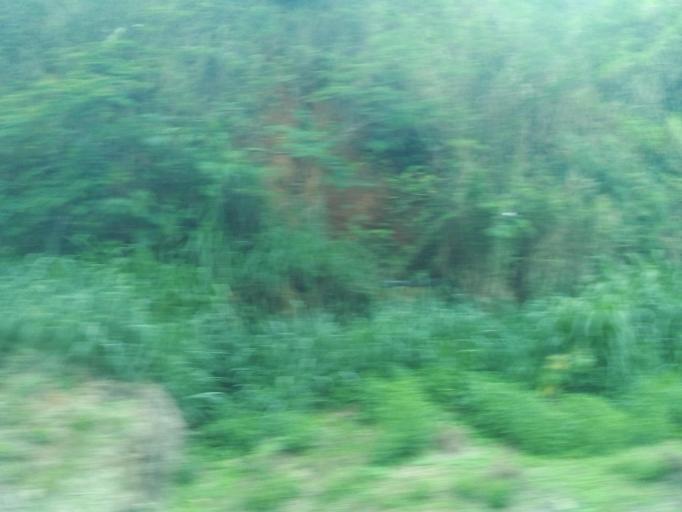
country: BR
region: Minas Gerais
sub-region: Nova Era
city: Nova Era
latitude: -19.7413
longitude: -43.0183
